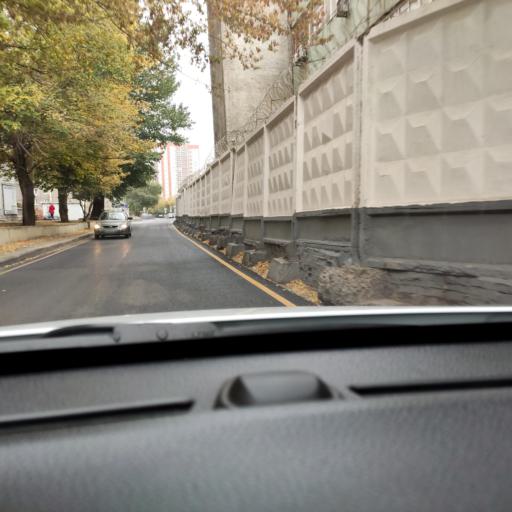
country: RU
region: Voronezj
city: Voronezh
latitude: 51.6695
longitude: 39.1815
